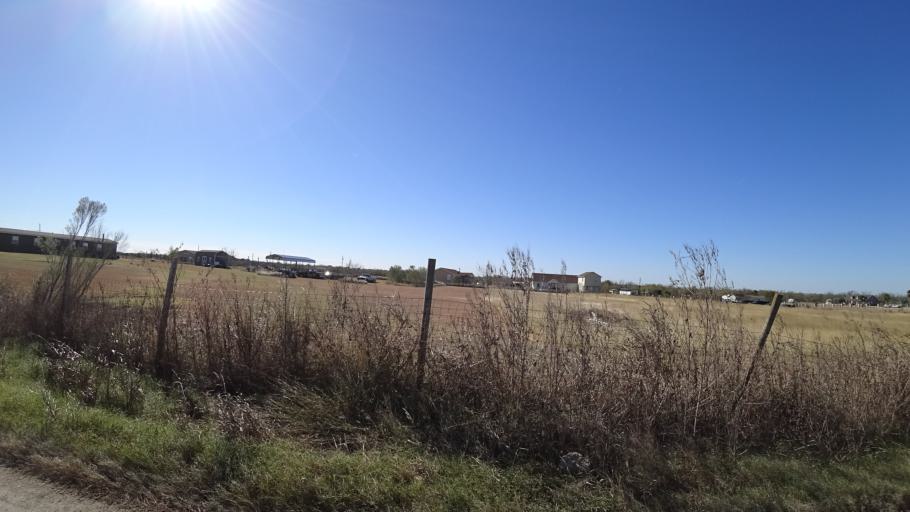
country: US
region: Texas
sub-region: Travis County
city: Garfield
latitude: 30.0986
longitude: -97.6186
